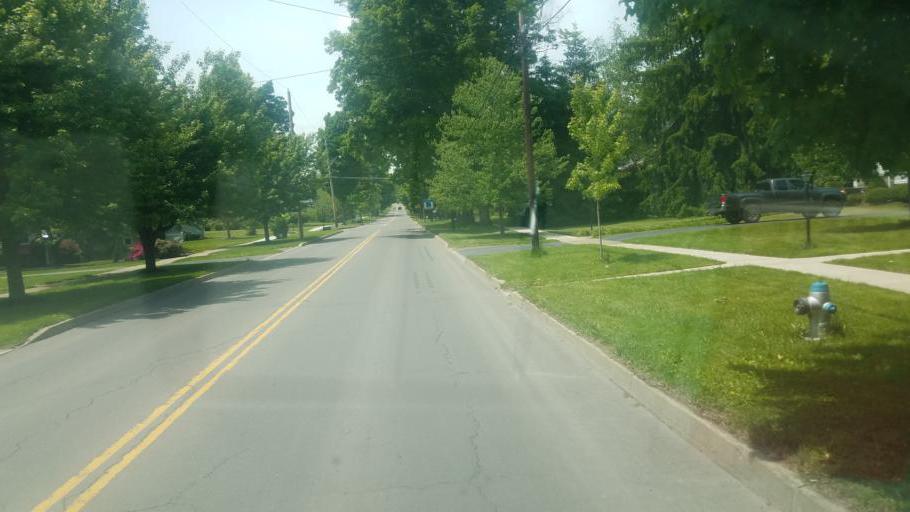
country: US
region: Pennsylvania
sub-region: Tioga County
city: Wellsboro
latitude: 41.7441
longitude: -77.3080
